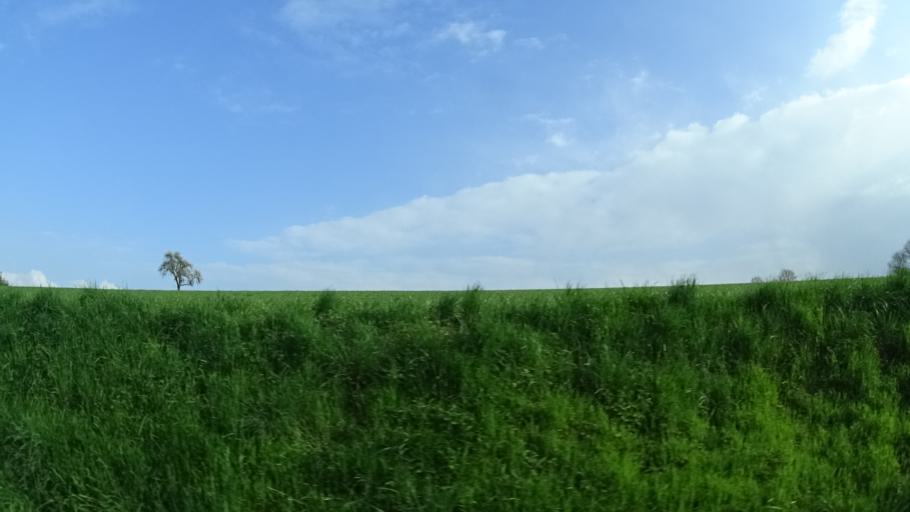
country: DE
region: Rheinland-Pfalz
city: Bockenau
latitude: 49.8412
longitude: 7.6998
